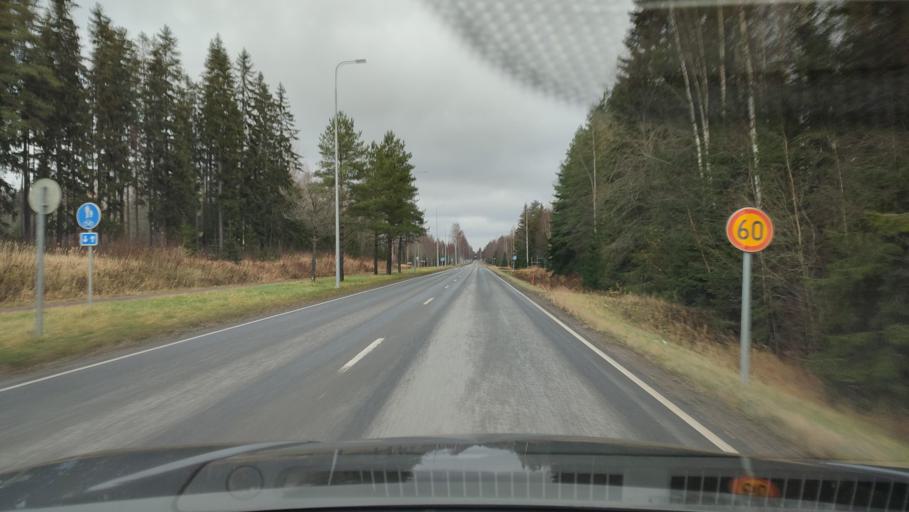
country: FI
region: Southern Ostrobothnia
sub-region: Suupohja
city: Kauhajoki
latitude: 62.4084
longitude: 22.1658
